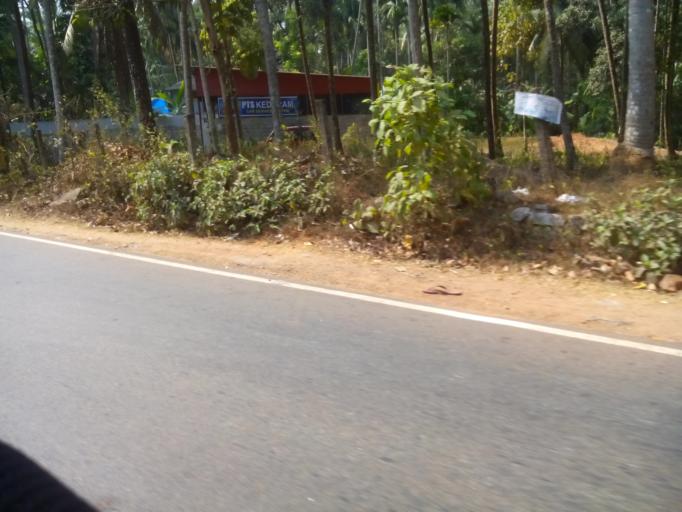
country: IN
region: Kerala
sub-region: Kozhikode
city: Naduvannur
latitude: 11.5740
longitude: 75.7566
